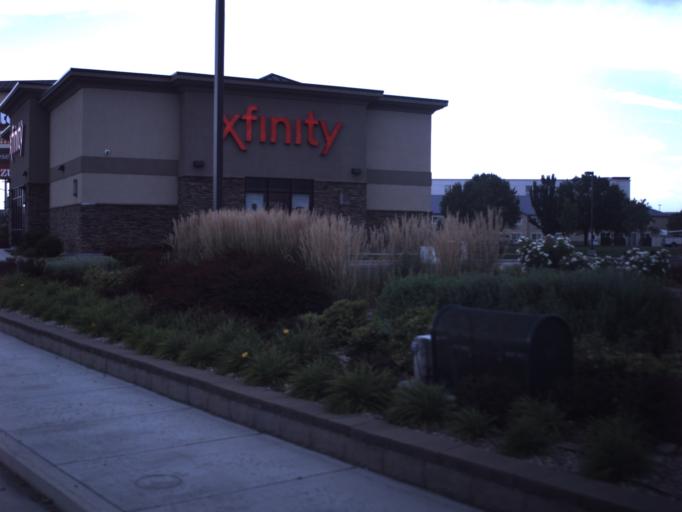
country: US
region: Utah
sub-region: Salt Lake County
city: Draper
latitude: 40.5290
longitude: -111.8898
